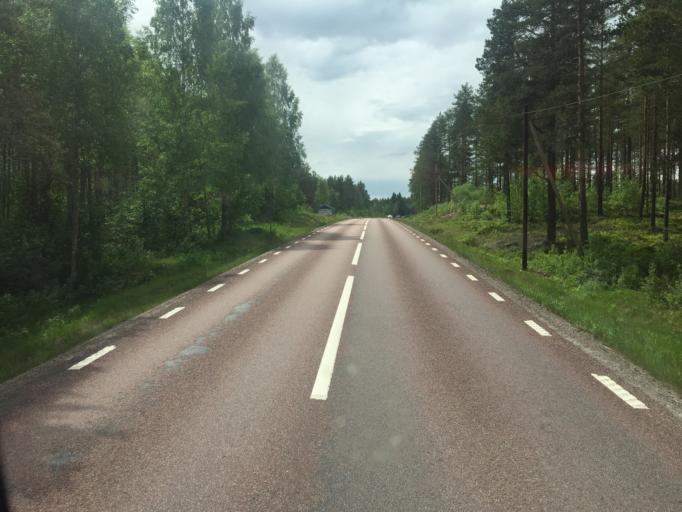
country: SE
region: Dalarna
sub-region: Vansbro Kommun
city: Vansbro
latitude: 60.5085
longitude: 14.1882
